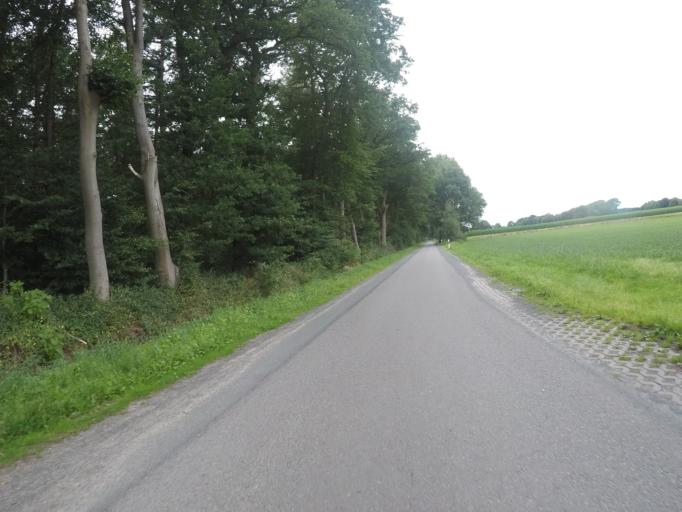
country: DE
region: Lower Saxony
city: Himmelpforten
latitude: 53.6082
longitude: 9.3237
